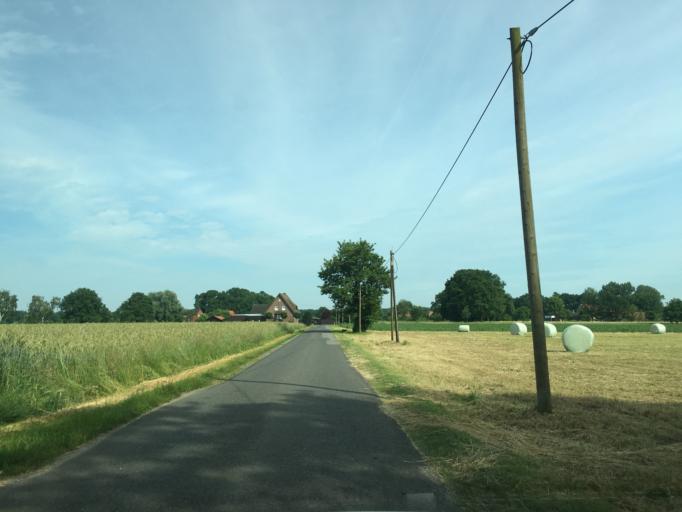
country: DE
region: North Rhine-Westphalia
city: Ludinghausen
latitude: 51.7662
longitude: 7.4693
